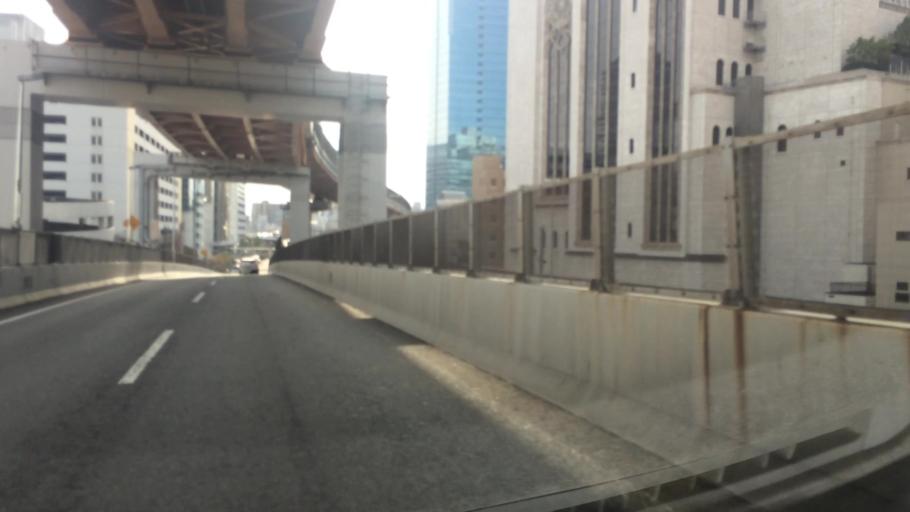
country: JP
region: Hyogo
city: Kobe
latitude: 34.6825
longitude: 135.1833
